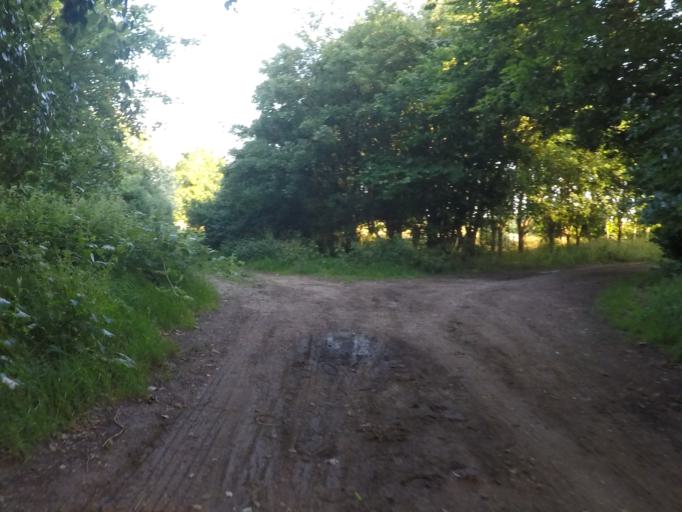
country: GB
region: England
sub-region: Oxfordshire
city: Stonesfield
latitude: 51.8776
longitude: -1.4476
